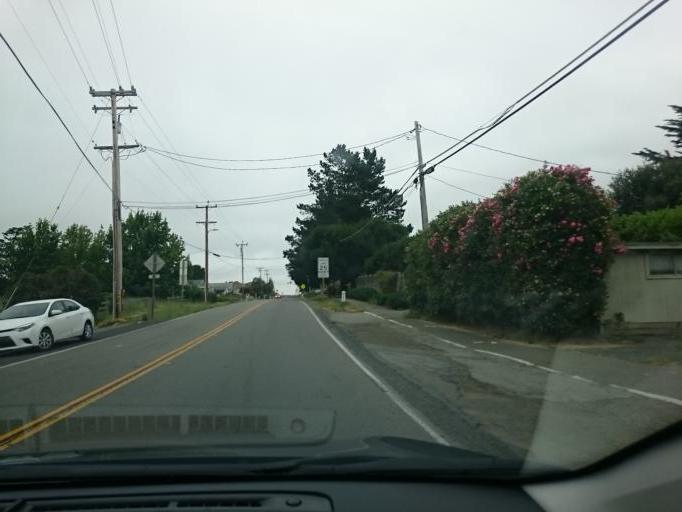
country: US
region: California
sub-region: Marin County
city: Inverness
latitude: 38.0693
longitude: -122.8060
